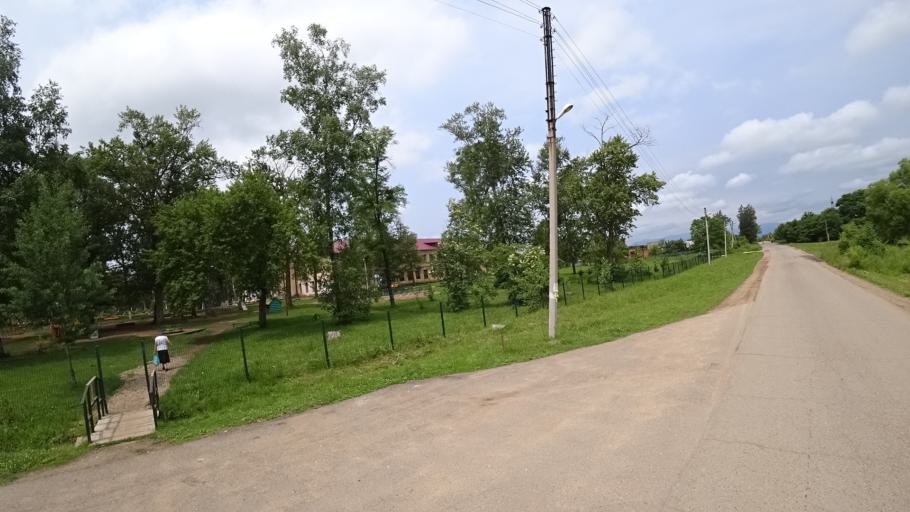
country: RU
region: Primorskiy
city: Novosysoyevka
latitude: 44.2296
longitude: 133.3609
